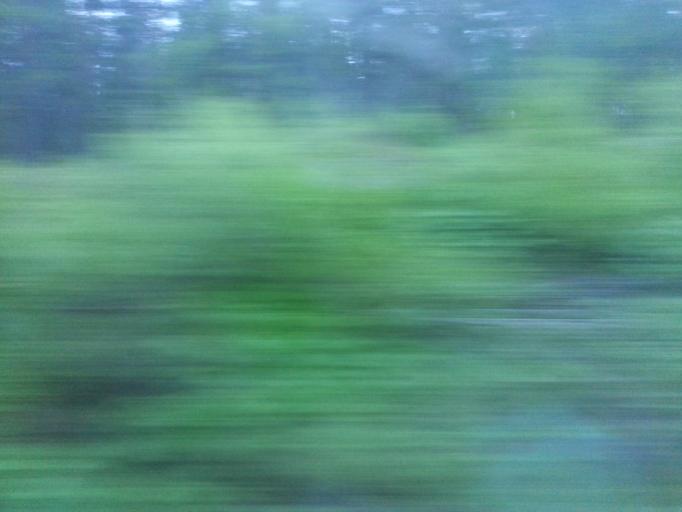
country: NO
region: Oppland
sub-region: Dovre
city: Dombas
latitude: 62.0859
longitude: 9.1423
